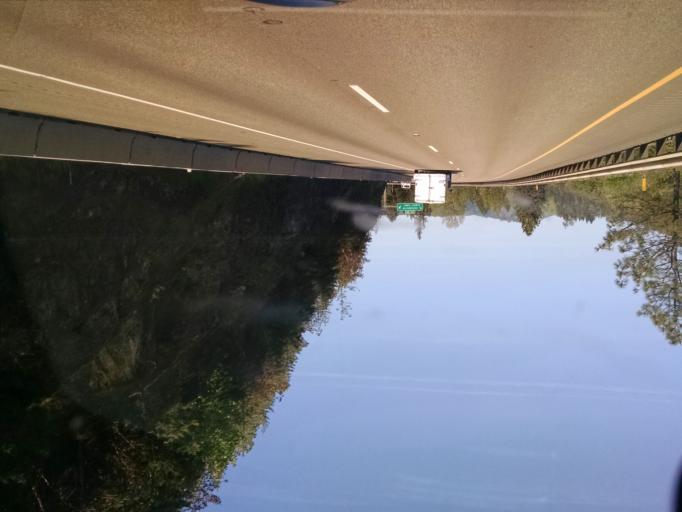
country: US
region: Oregon
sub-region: Douglas County
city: Canyonville
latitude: 42.9479
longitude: -123.2995
